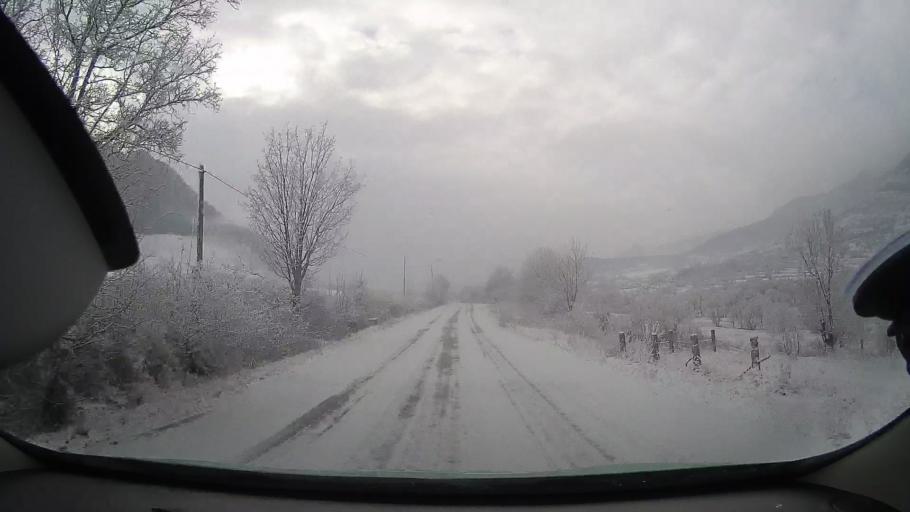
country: RO
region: Alba
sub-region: Comuna Rimetea
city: Rimetea
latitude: 46.4631
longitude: 23.5726
